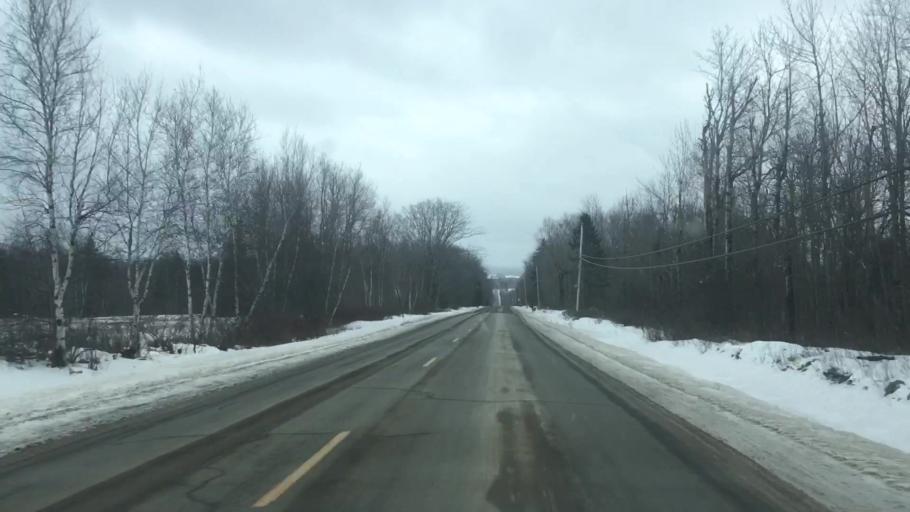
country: US
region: Maine
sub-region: Washington County
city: East Machias
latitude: 44.9776
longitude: -67.4520
